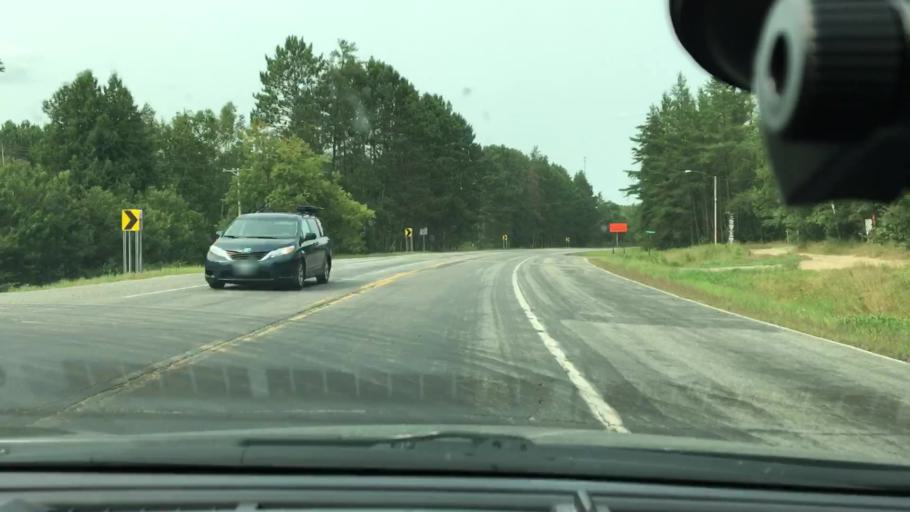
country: US
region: Minnesota
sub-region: Crow Wing County
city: Cross Lake
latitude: 46.7430
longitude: -93.9666
